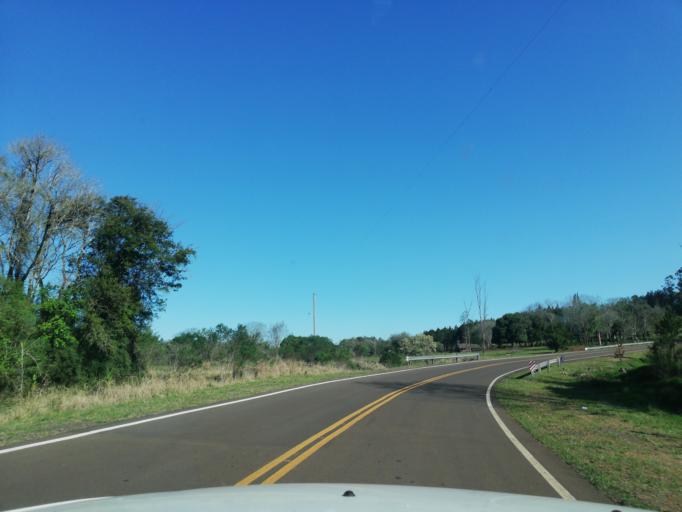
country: AR
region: Misiones
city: Arroyo del Medio
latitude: -27.6746
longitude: -55.3992
